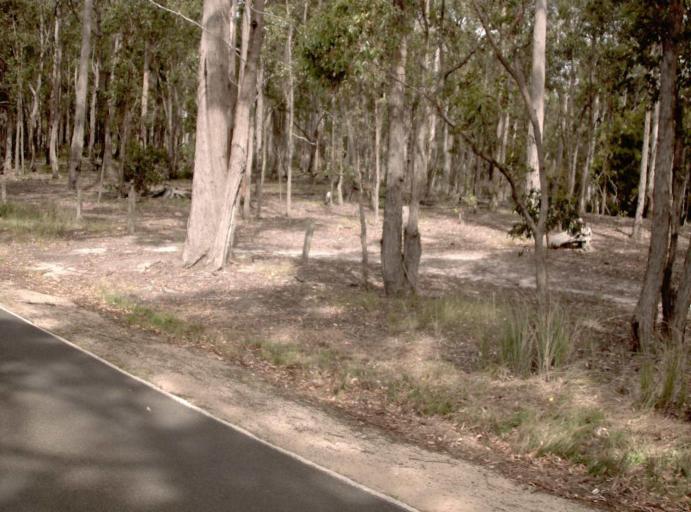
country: AU
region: Victoria
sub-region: Latrobe
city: Traralgon
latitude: -38.3795
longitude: 146.7726
